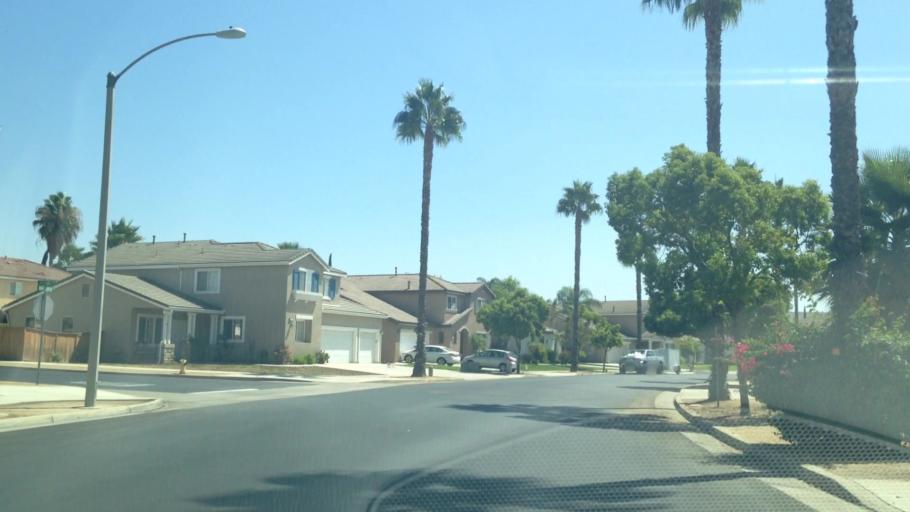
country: US
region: California
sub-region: Riverside County
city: Home Gardens
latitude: 33.8608
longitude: -117.4457
